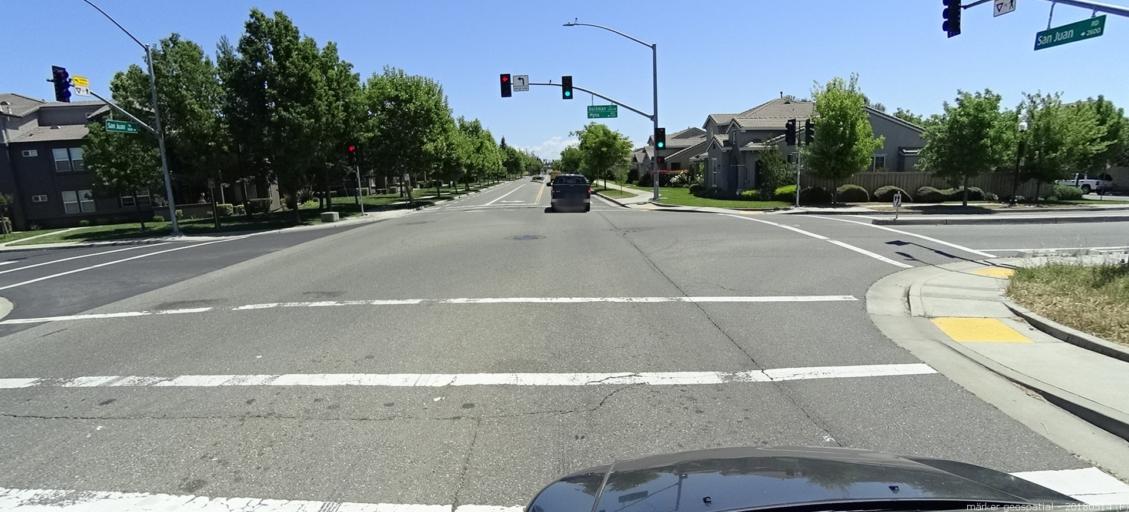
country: US
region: California
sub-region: Yolo County
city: West Sacramento
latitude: 38.6277
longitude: -121.5250
